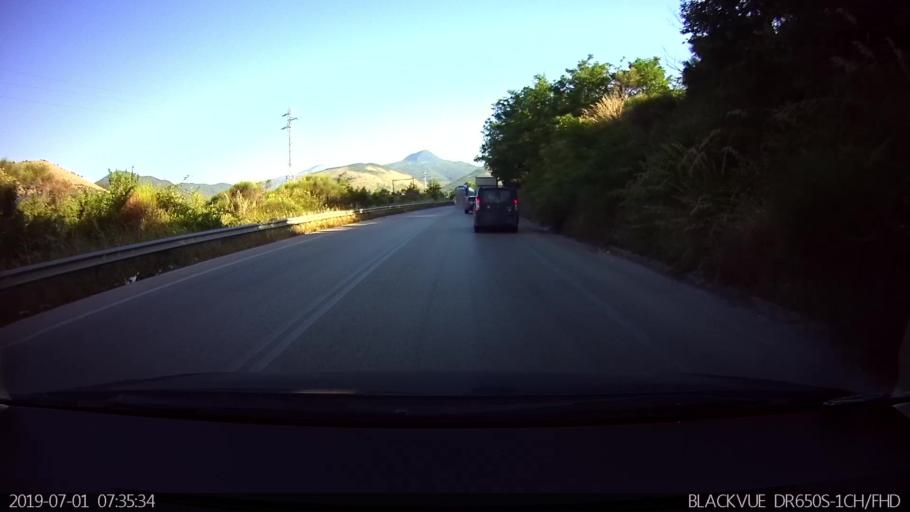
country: IT
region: Latium
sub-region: Provincia di Latina
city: Prossedi
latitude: 41.5255
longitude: 13.2691
